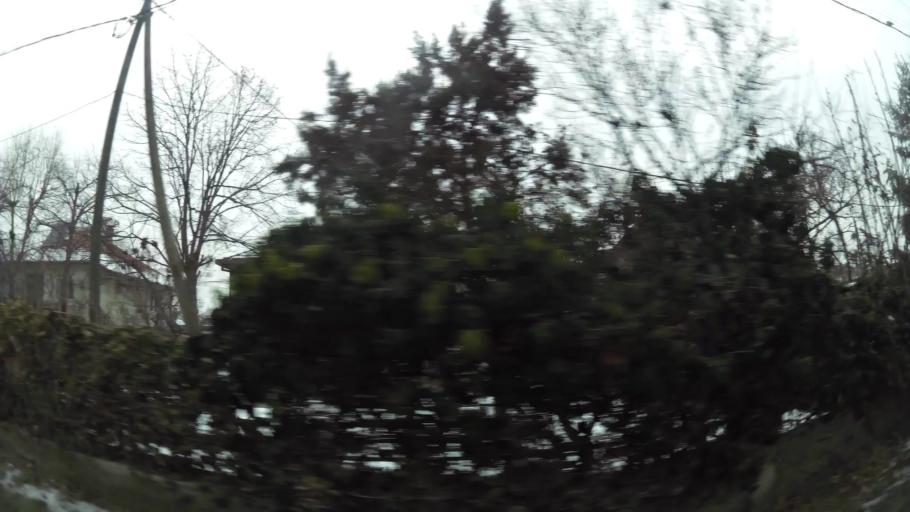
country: MK
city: Kondovo
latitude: 42.0452
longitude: 21.3496
